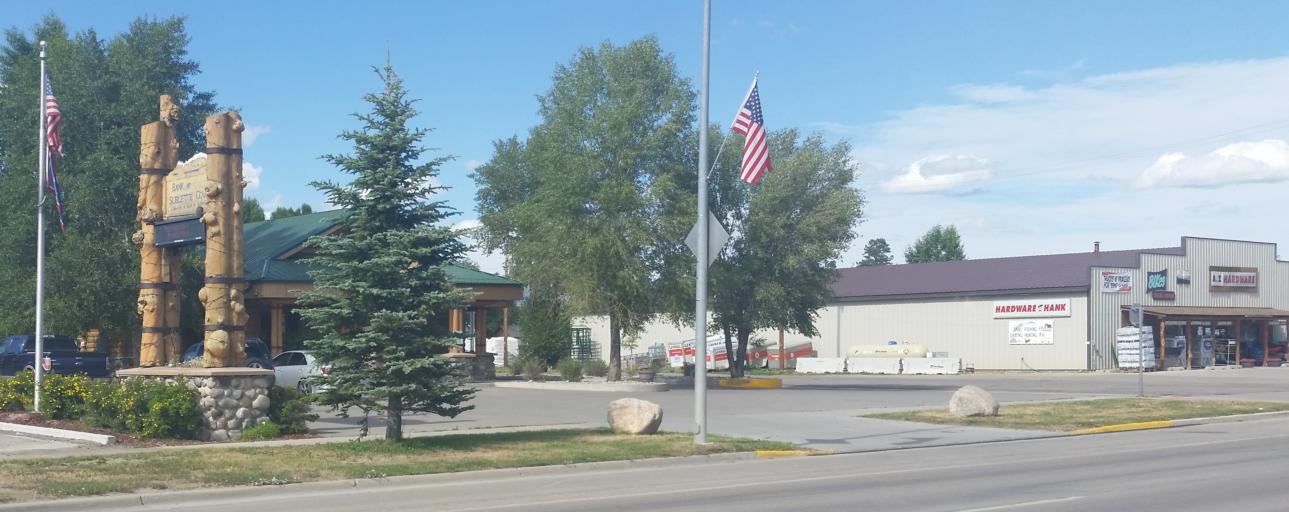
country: US
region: Wyoming
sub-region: Sublette County
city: Pinedale
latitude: 42.8665
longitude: -109.8730
